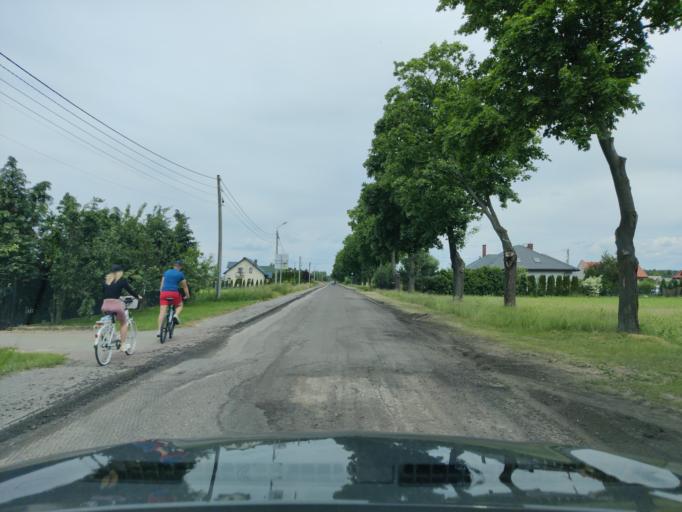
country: PL
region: Masovian Voivodeship
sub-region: Powiat wyszkowski
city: Rzasnik
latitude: 52.6903
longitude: 21.4216
